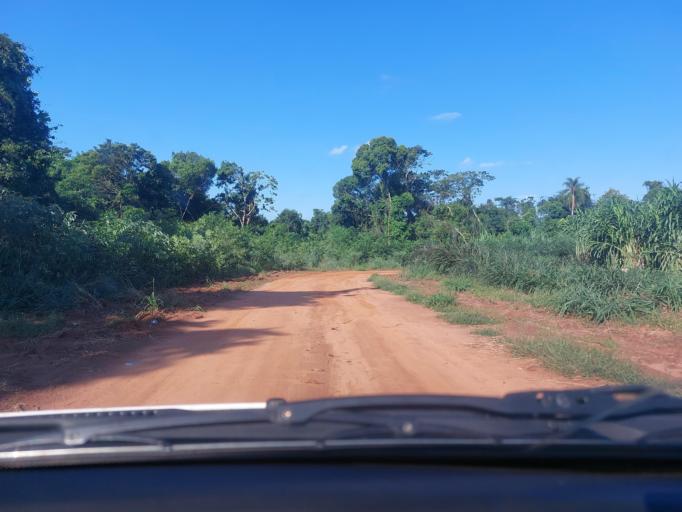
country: PY
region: San Pedro
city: Guayaybi
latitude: -24.5223
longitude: -56.5459
